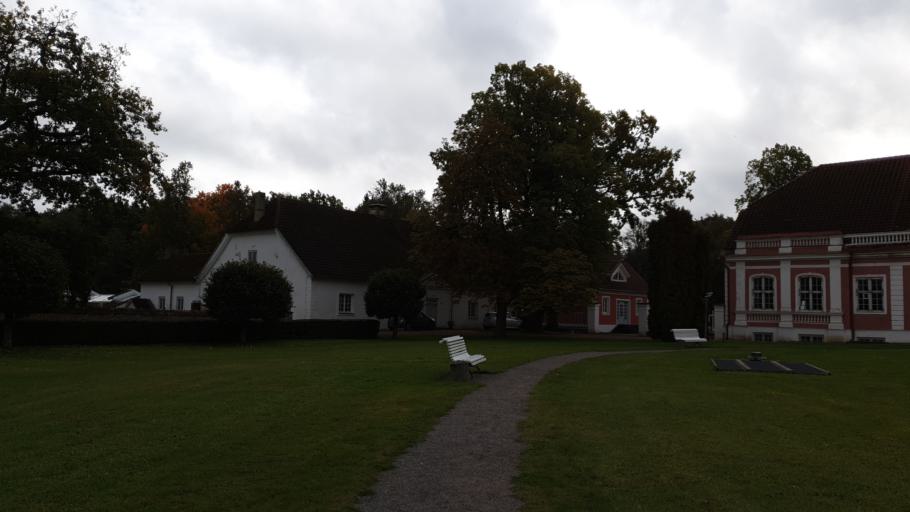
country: EE
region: Laeaene-Virumaa
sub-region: Haljala vald
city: Haljala
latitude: 59.5374
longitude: 26.0845
